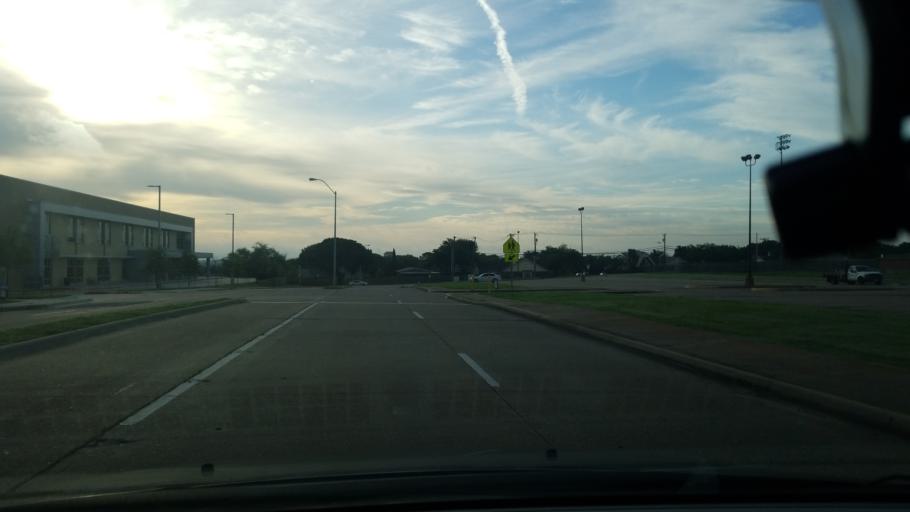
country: US
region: Texas
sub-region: Dallas County
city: Mesquite
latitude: 32.7623
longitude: -96.6331
